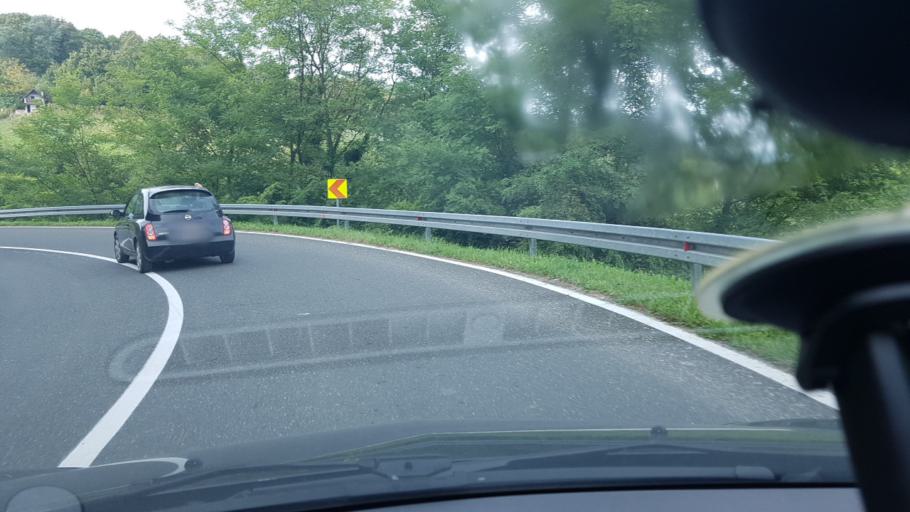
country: HR
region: Varazdinska
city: Ljubescica
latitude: 46.1403
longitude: 16.3610
